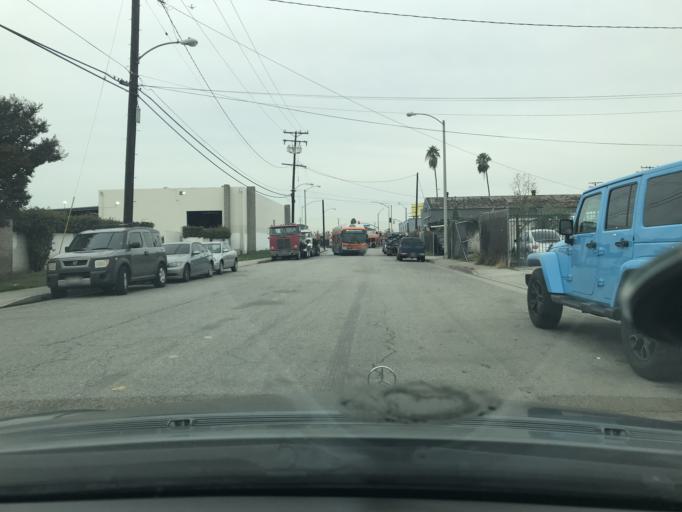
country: US
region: California
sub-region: Los Angeles County
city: Cudahy
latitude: 33.9583
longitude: -118.1833
